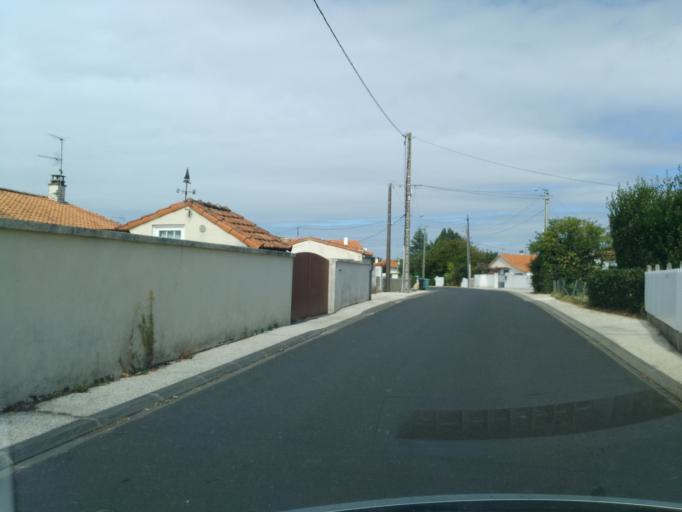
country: FR
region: Poitou-Charentes
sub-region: Departement de la Charente-Maritime
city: Saint-Palais-sur-Mer
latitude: 45.6533
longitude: -1.0787
